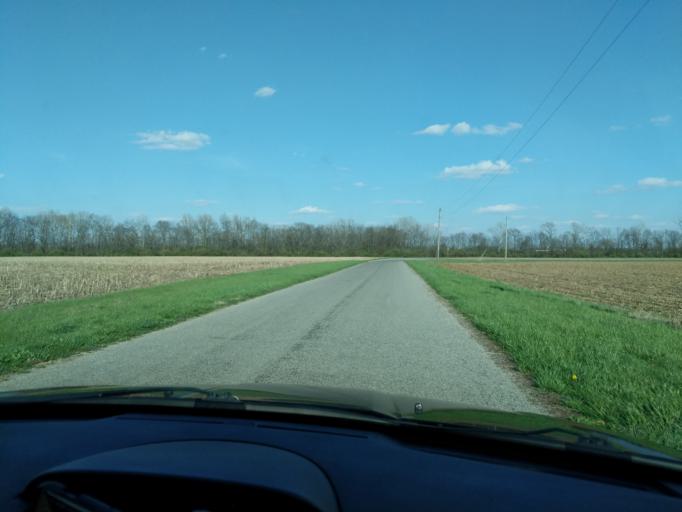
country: US
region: Ohio
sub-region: Champaign County
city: Urbana
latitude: 40.1151
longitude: -83.8068
